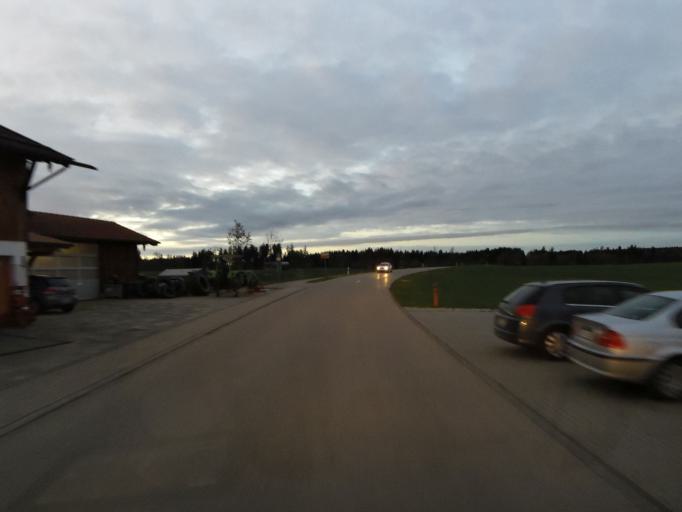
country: DE
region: Bavaria
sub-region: Upper Bavaria
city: Valley
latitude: 47.9108
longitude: 11.7650
